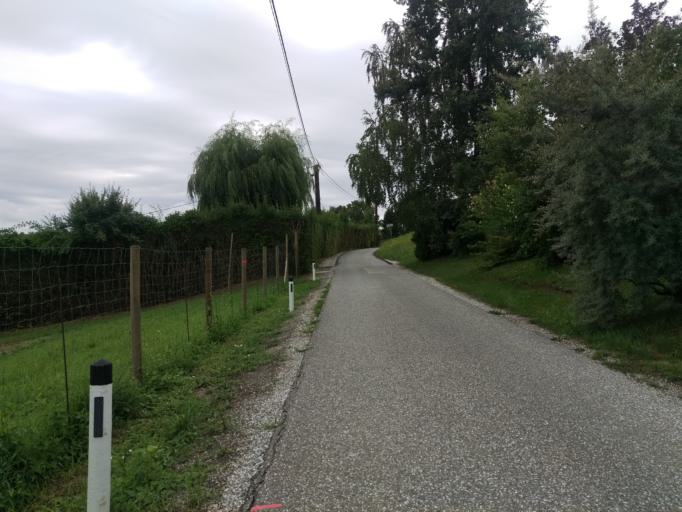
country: AT
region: Styria
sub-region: Politischer Bezirk Graz-Umgebung
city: Raaba
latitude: 47.0503
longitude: 15.4991
